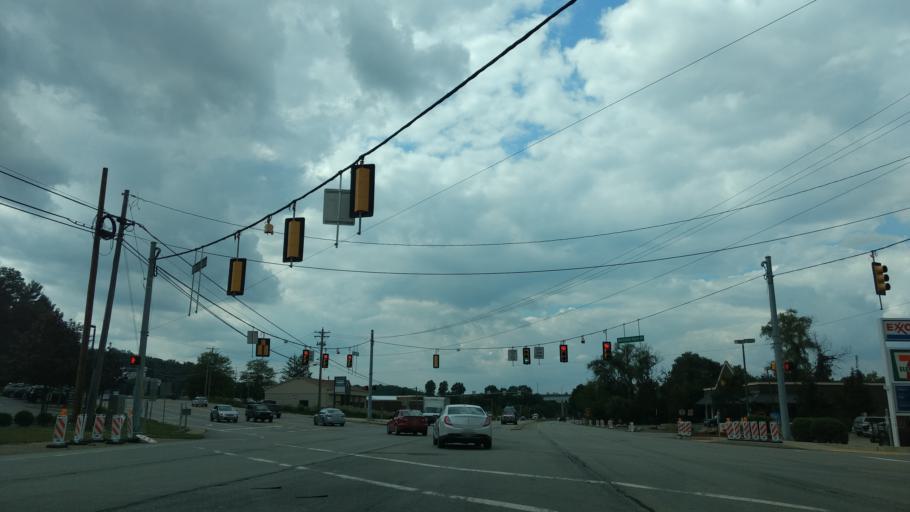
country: US
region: Pennsylvania
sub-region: Allegheny County
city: Bradford Woods
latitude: 40.6550
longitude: -80.0866
